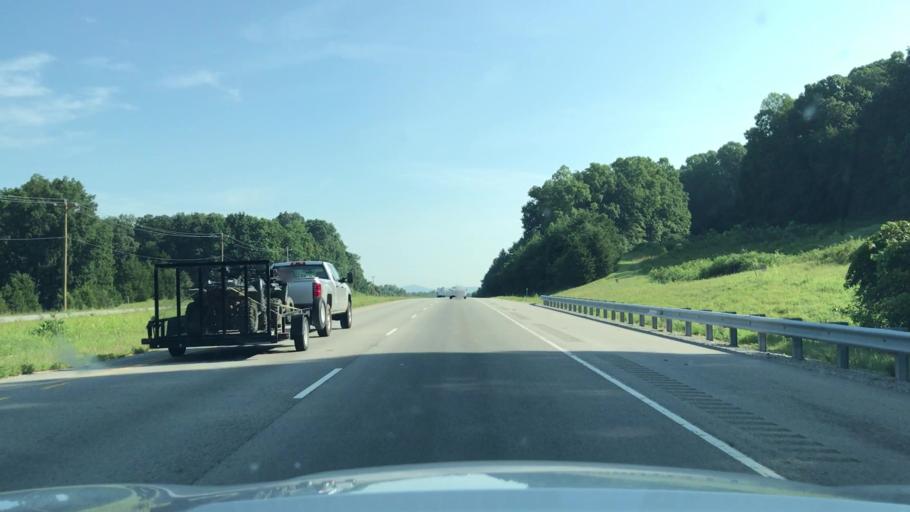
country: US
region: Tennessee
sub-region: Overton County
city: Livingston
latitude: 36.3107
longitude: -85.3651
